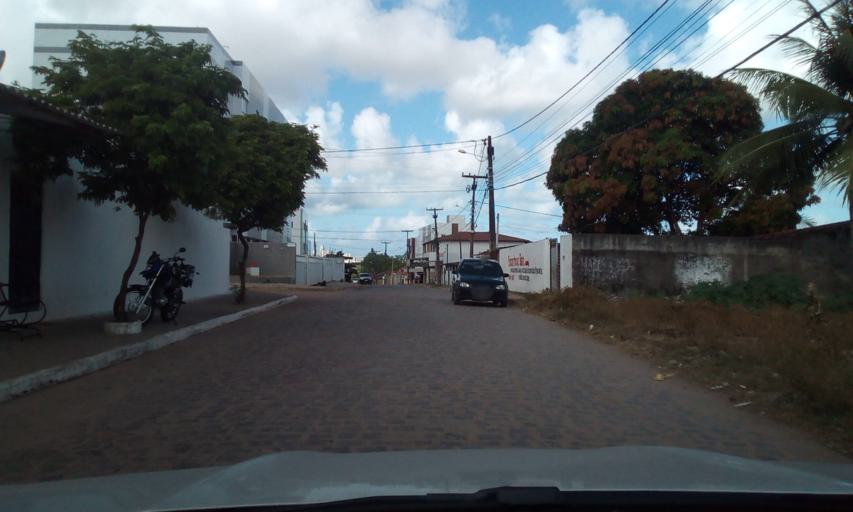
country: BR
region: Paraiba
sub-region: Joao Pessoa
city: Joao Pessoa
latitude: -7.1772
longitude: -34.8511
